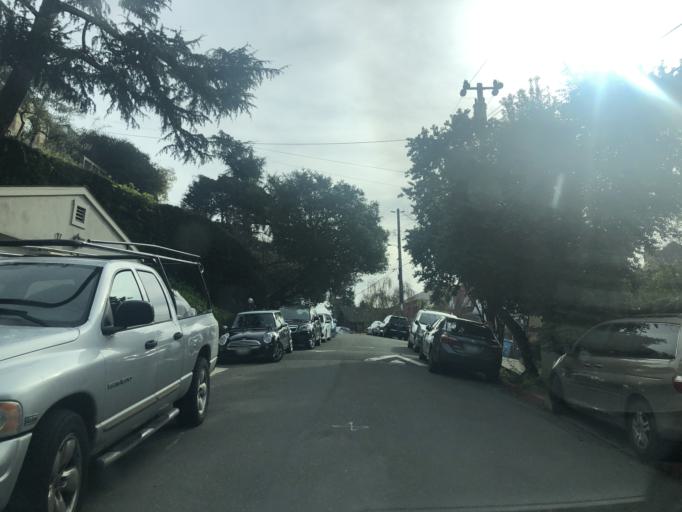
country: US
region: California
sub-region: Alameda County
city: Berkeley
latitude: 37.8569
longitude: -122.2434
